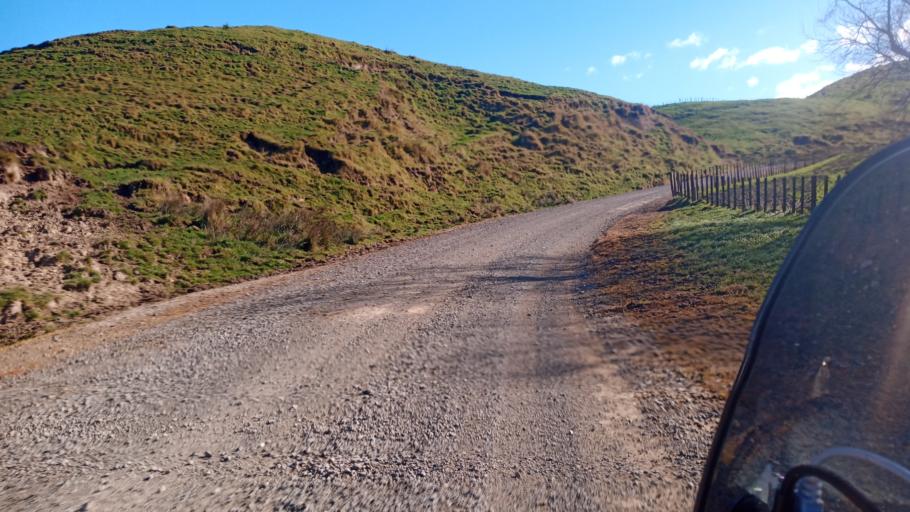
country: NZ
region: Hawke's Bay
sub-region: Wairoa District
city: Wairoa
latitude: -38.7788
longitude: 177.2636
